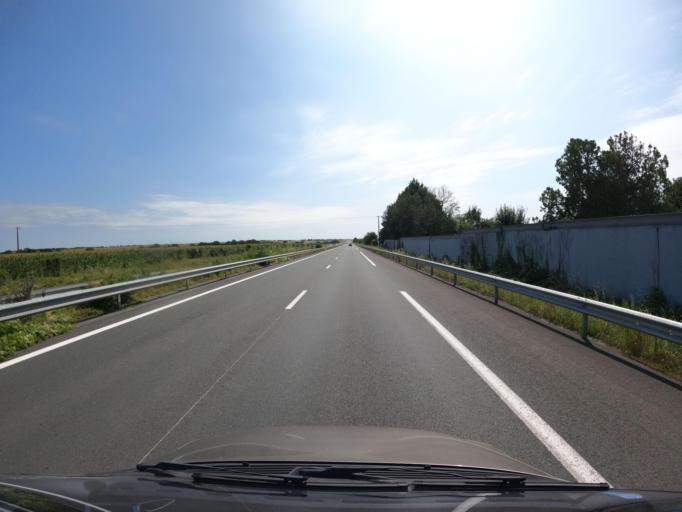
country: FR
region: Poitou-Charentes
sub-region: Departement des Deux-Sevres
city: Mauze-sur-le-Mignon
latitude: 46.2045
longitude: -0.7237
